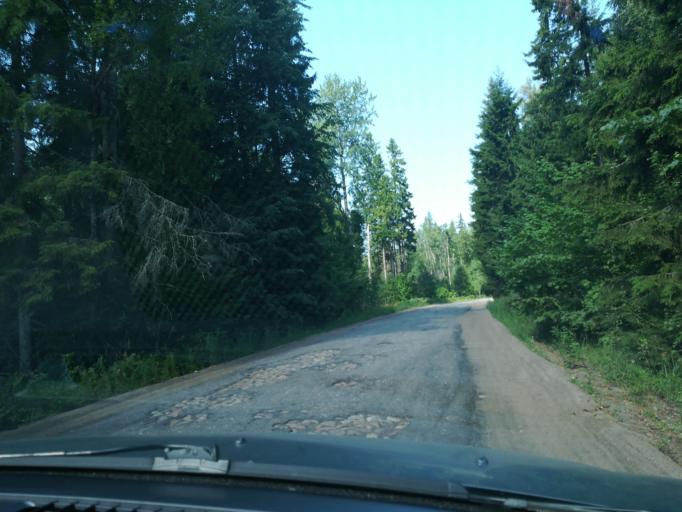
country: RU
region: Leningrad
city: Ust'-Luga
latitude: 59.7227
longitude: 28.2026
